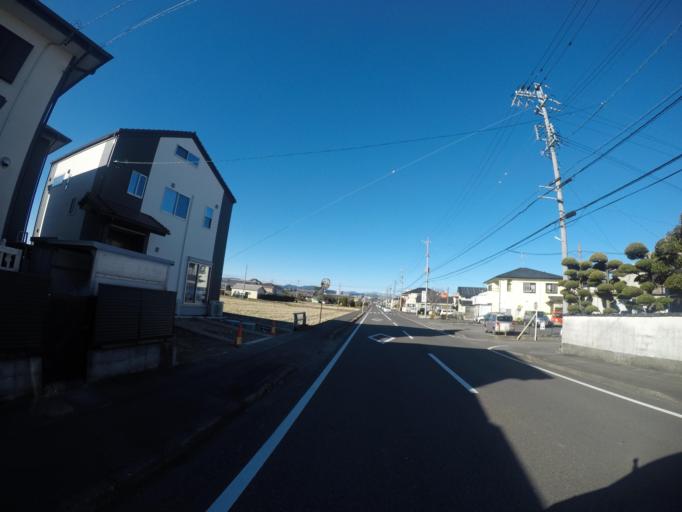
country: JP
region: Shizuoka
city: Fujieda
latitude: 34.8354
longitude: 138.2573
